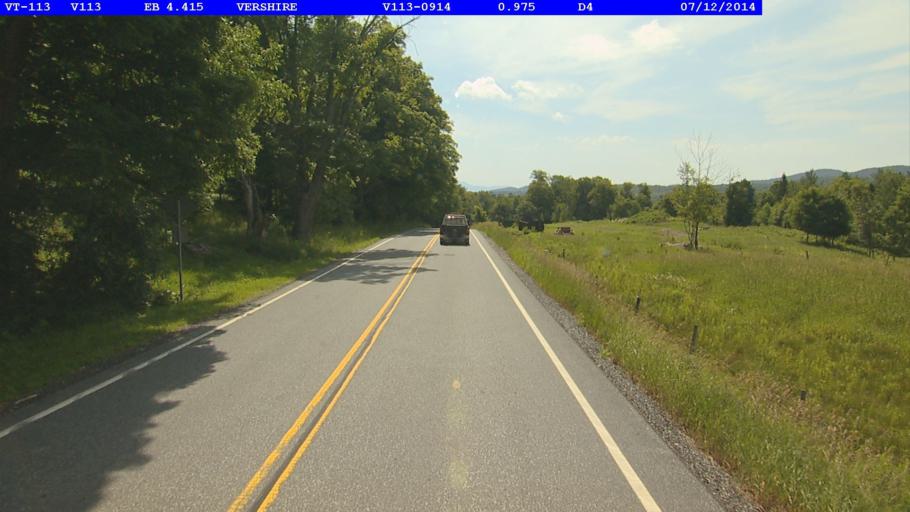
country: US
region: Vermont
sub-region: Orange County
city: Chelsea
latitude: 43.9859
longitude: -72.3674
